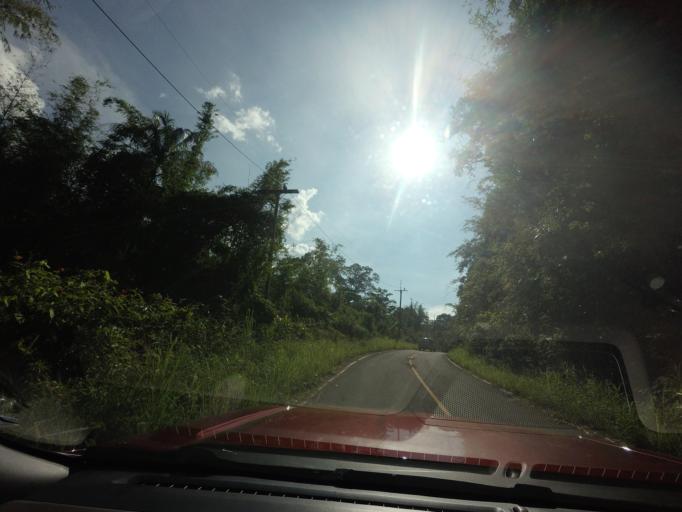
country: TH
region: Narathiwat
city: Si Sakhon
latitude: 6.0614
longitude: 101.3765
